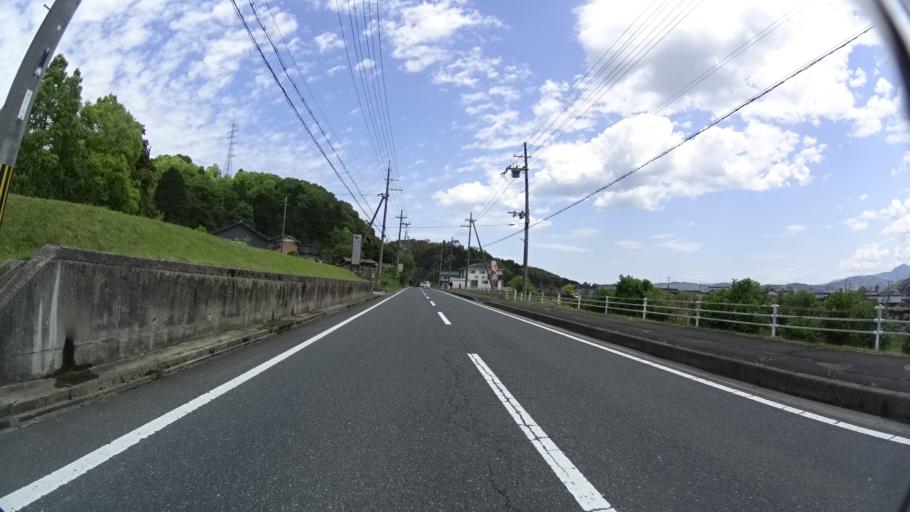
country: JP
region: Kyoto
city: Miyazu
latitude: 35.5728
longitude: 135.1551
